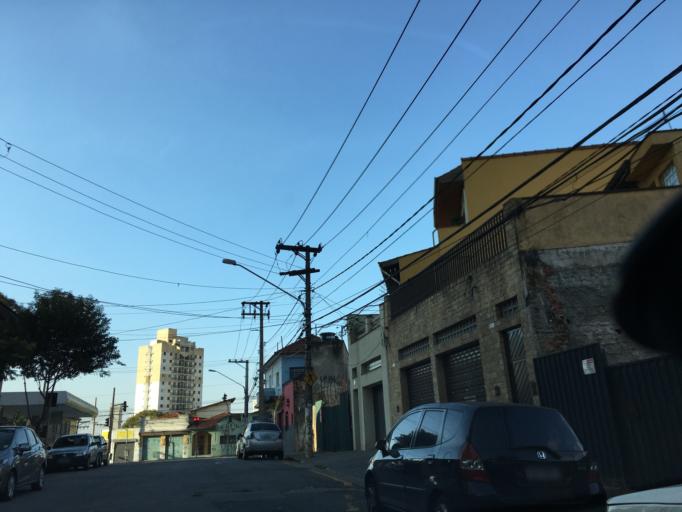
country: BR
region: Sao Paulo
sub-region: Sao Paulo
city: Sao Paulo
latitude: -23.4907
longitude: -46.6363
